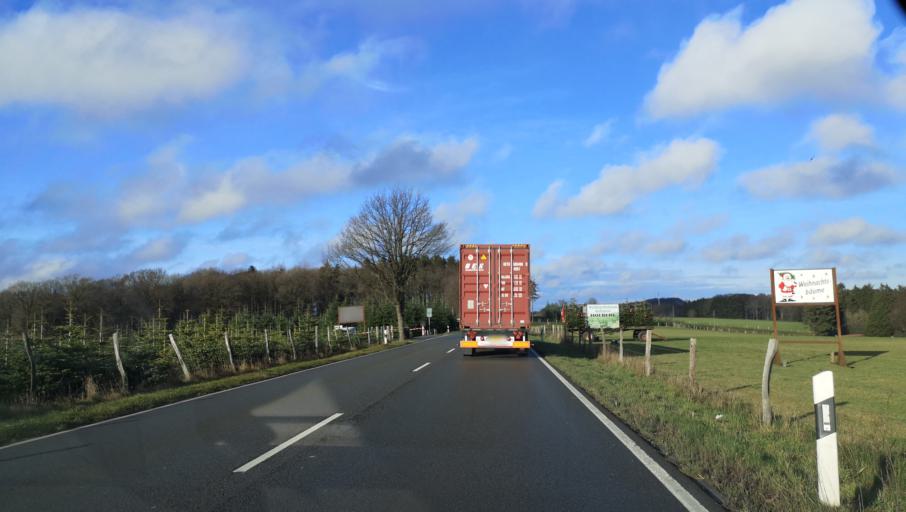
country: DE
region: North Rhine-Westphalia
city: Radevormwald
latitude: 51.2241
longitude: 7.3712
